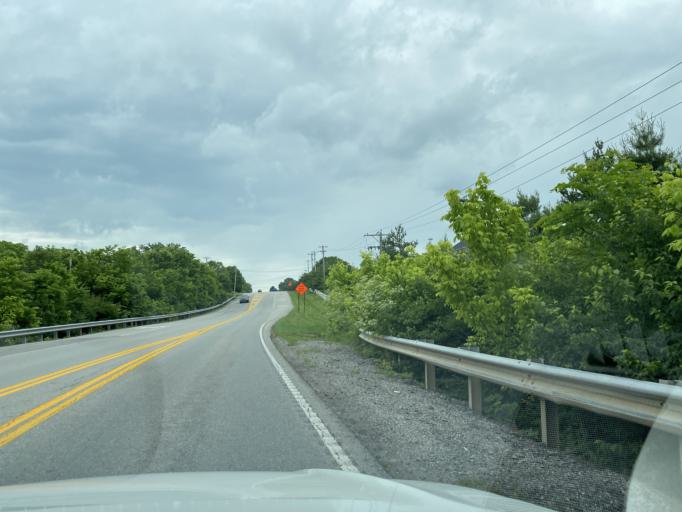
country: US
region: Kentucky
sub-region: Scott County
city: Georgetown
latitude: 38.2177
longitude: -84.5239
